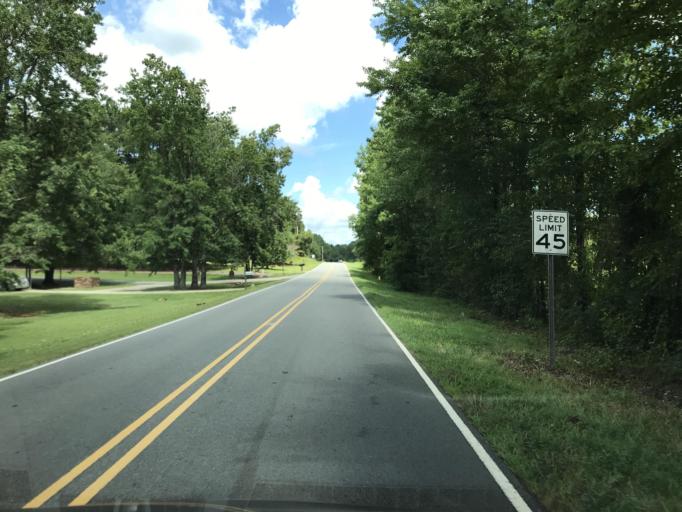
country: US
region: North Carolina
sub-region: Lincoln County
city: Lincolnton
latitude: 35.5042
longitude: -81.2325
